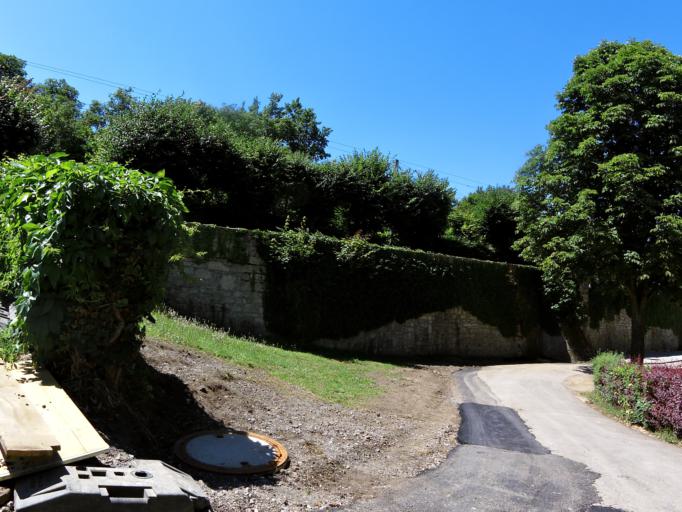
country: DE
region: Bavaria
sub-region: Regierungsbezirk Unterfranken
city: Ochsenfurt
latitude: 49.6635
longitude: 10.0621
